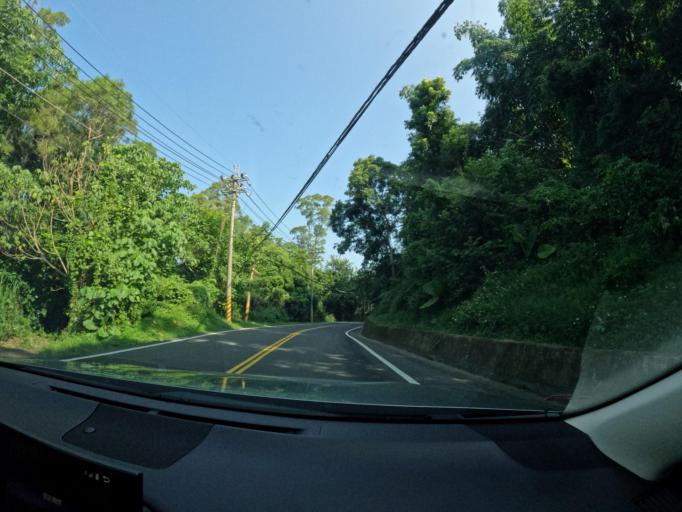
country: TW
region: Taiwan
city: Yujing
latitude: 23.0756
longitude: 120.6122
